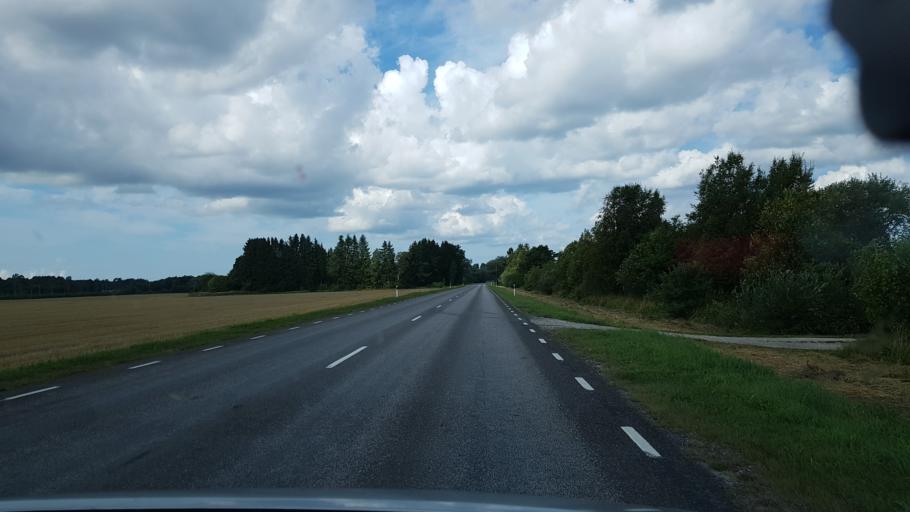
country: EE
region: Laeaene
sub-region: Ridala Parish
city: Uuemoisa
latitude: 58.8574
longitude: 23.6344
